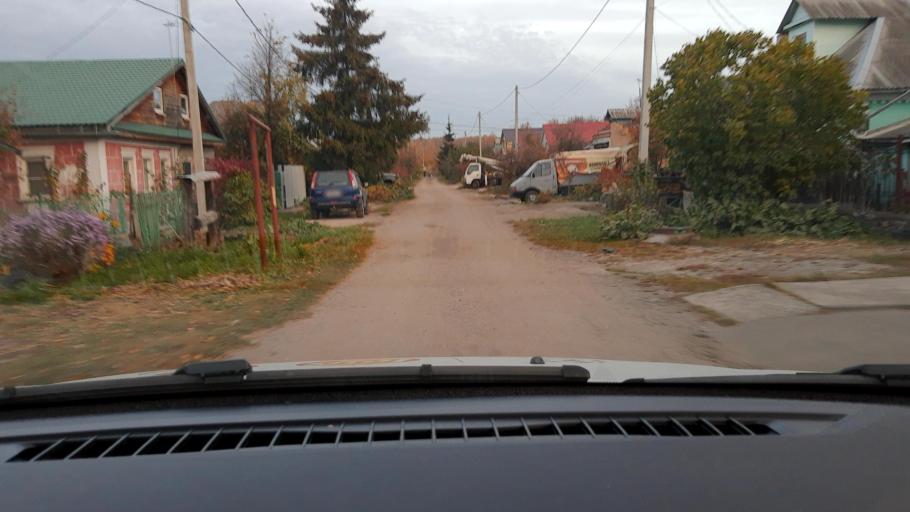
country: RU
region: Nizjnij Novgorod
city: Burevestnik
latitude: 56.2120
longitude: 43.8150
